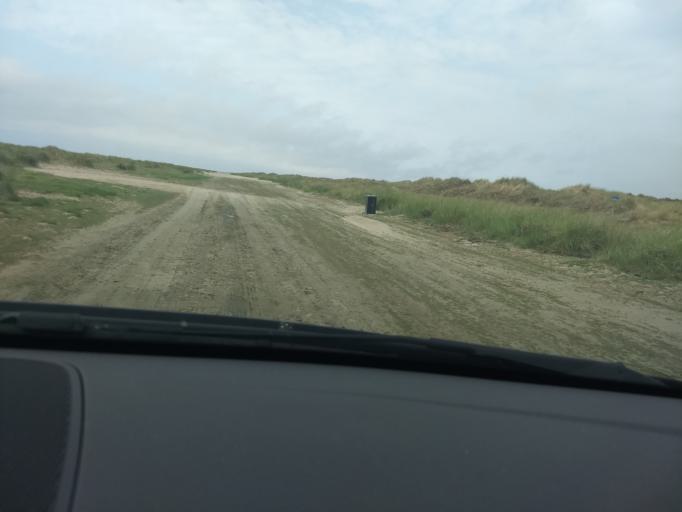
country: DK
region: South Denmark
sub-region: Fano Kommune
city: Nordby
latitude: 55.4093
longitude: 8.3856
